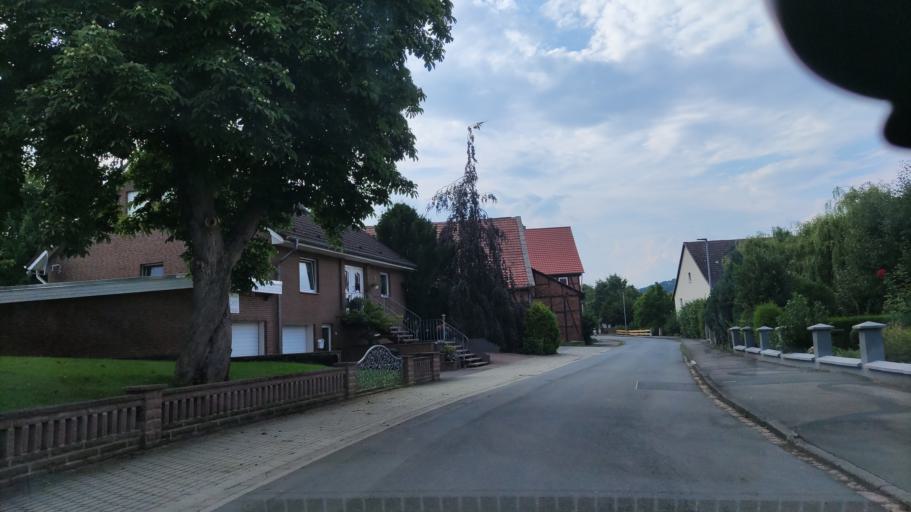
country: DE
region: Lower Saxony
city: Eimen
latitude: 51.8317
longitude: 9.7971
